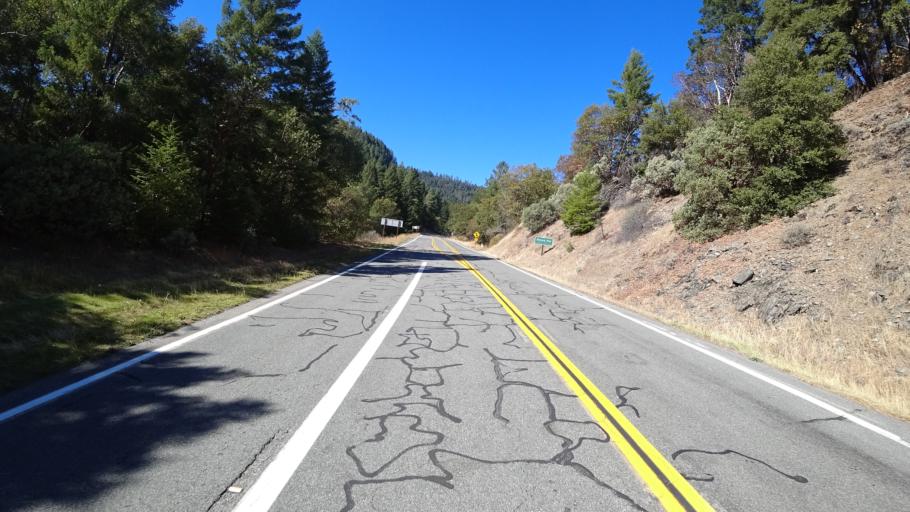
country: US
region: California
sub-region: Siskiyou County
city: Happy Camp
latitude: 41.3811
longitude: -123.4899
